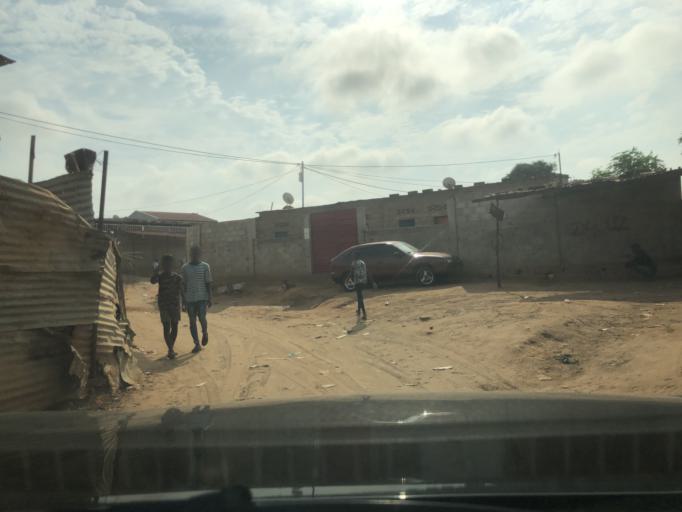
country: AO
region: Luanda
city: Luanda
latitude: -8.9375
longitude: 13.2383
